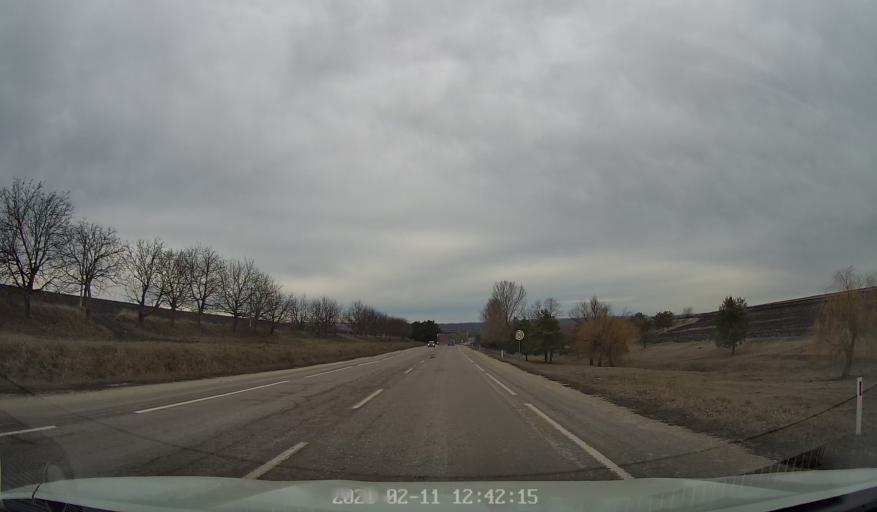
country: MD
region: Raionul Edinet
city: Edinet
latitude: 48.2211
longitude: 27.2251
